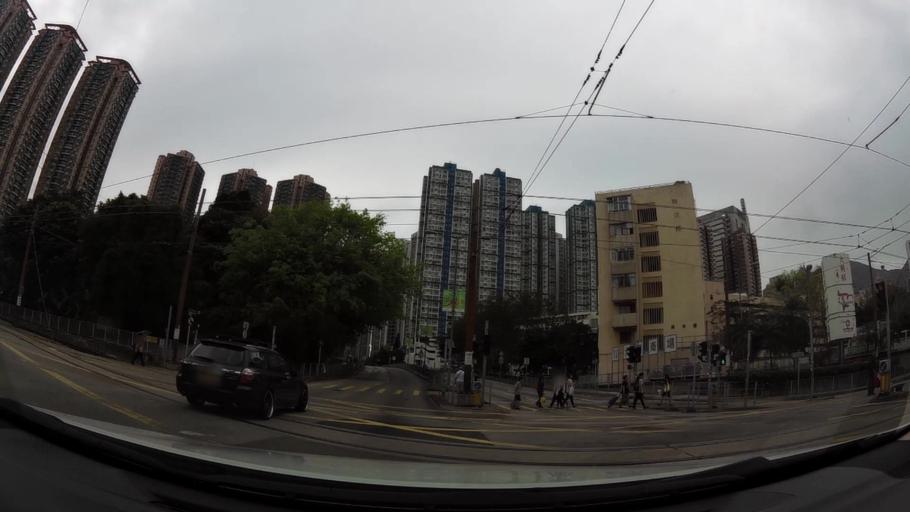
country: HK
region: Tuen Mun
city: Tuen Mun
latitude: 22.4030
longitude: 113.9729
